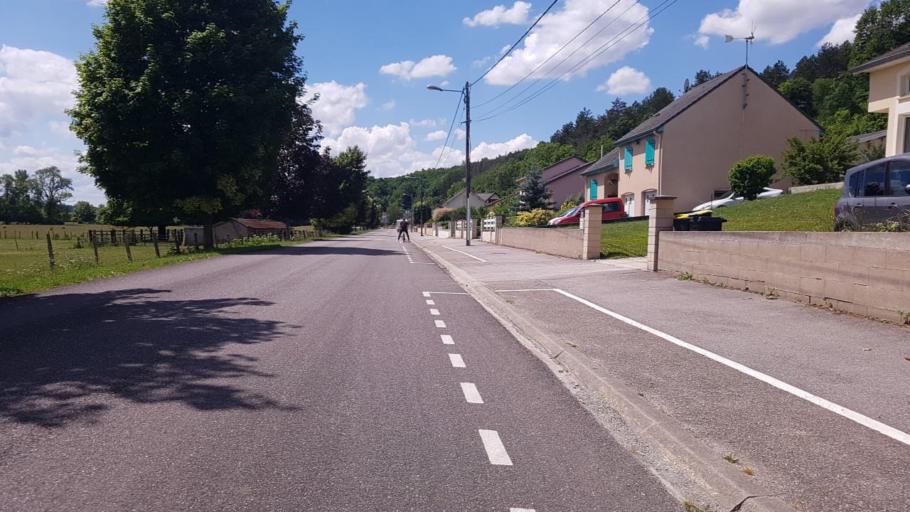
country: FR
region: Lorraine
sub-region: Departement de la Meuse
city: Vacon
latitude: 48.6820
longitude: 5.6123
